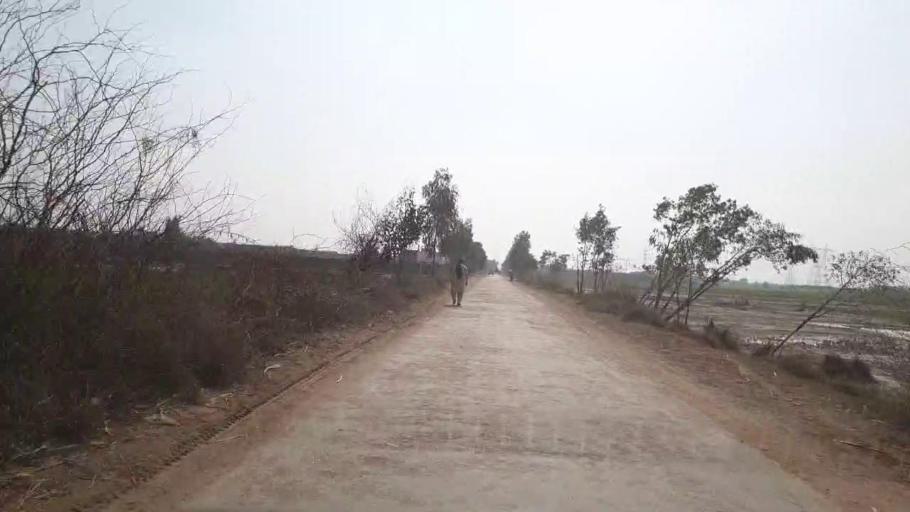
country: PK
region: Sindh
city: Bhit Shah
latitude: 25.7003
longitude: 68.5437
